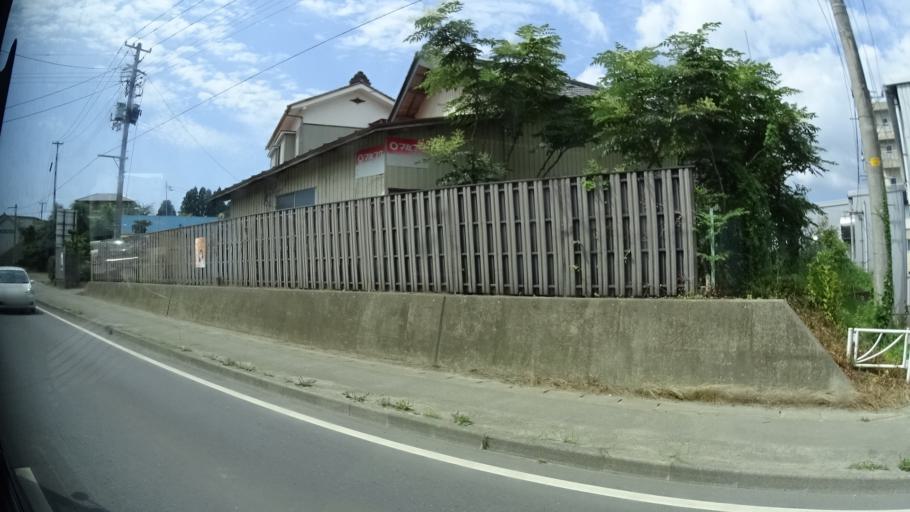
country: JP
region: Iwate
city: Ofunato
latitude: 38.8808
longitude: 141.5757
